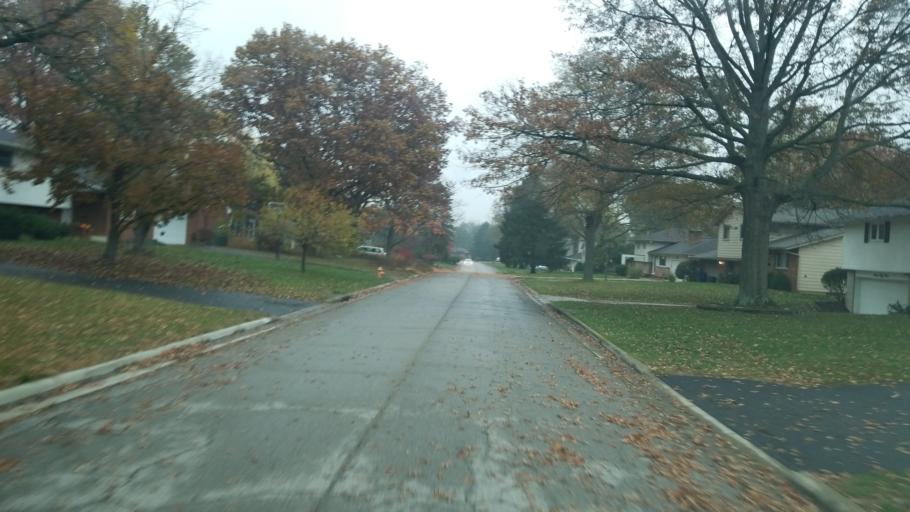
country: US
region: Ohio
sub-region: Franklin County
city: Worthington
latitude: 40.0481
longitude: -83.0402
